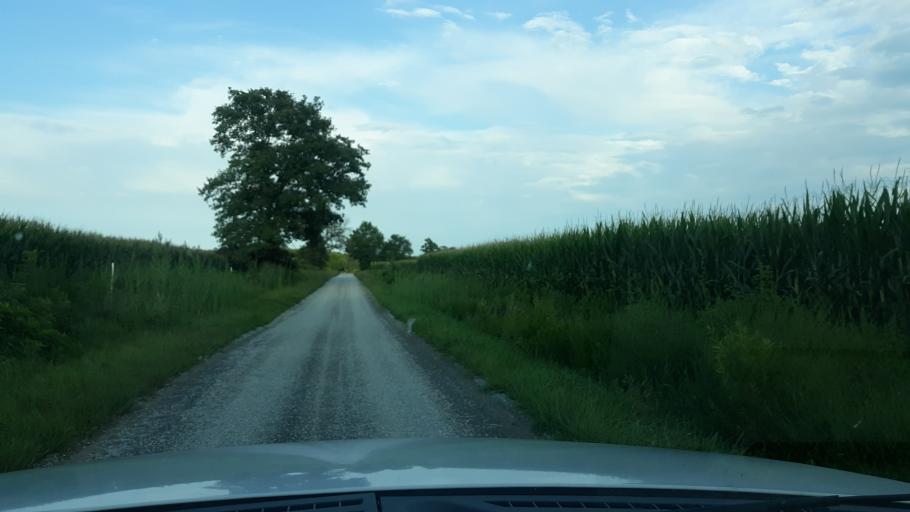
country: US
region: Illinois
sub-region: Saline County
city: Eldorado
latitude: 37.8343
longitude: -88.5145
